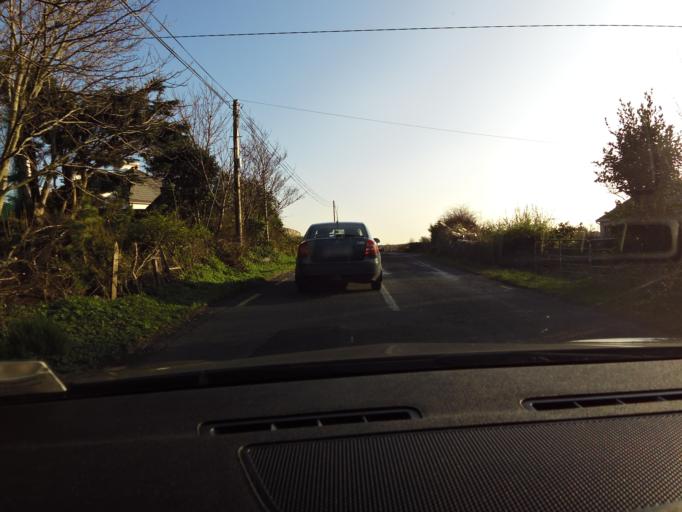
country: IE
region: Connaught
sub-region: County Galway
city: Oughterard
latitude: 53.3185
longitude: -9.5502
